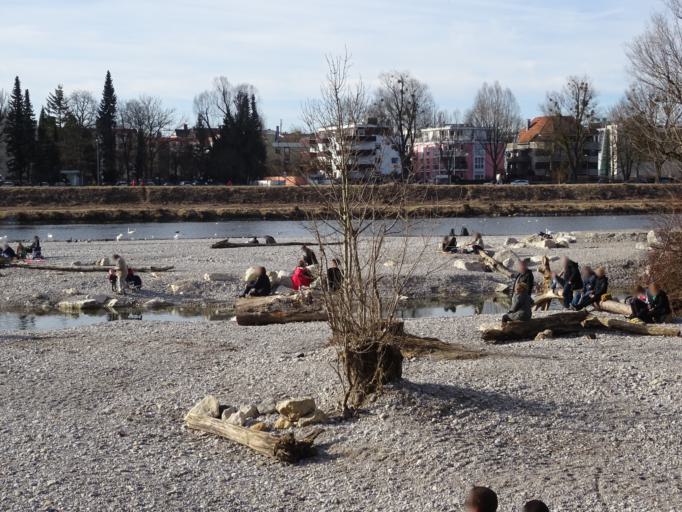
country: DE
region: Bavaria
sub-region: Upper Bavaria
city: Munich
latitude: 48.1029
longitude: 11.5524
